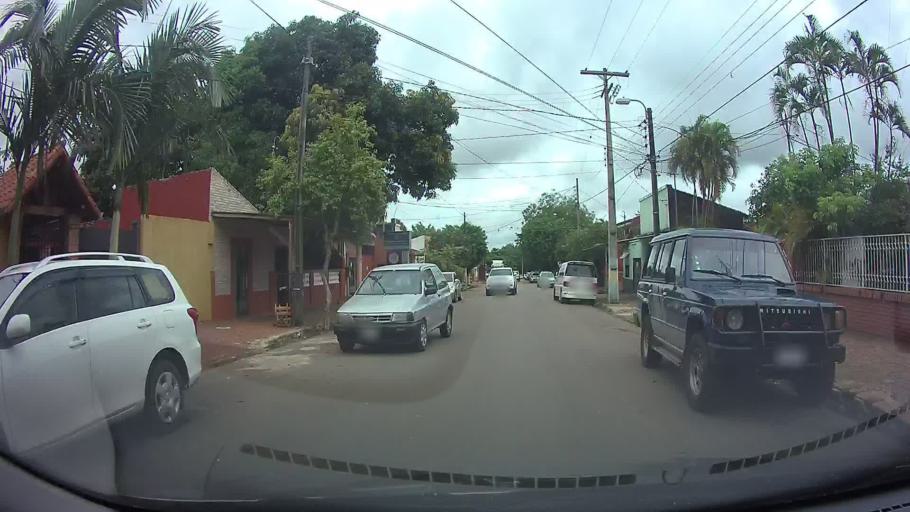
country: PY
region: Central
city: San Lorenzo
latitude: -25.2693
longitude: -57.4830
